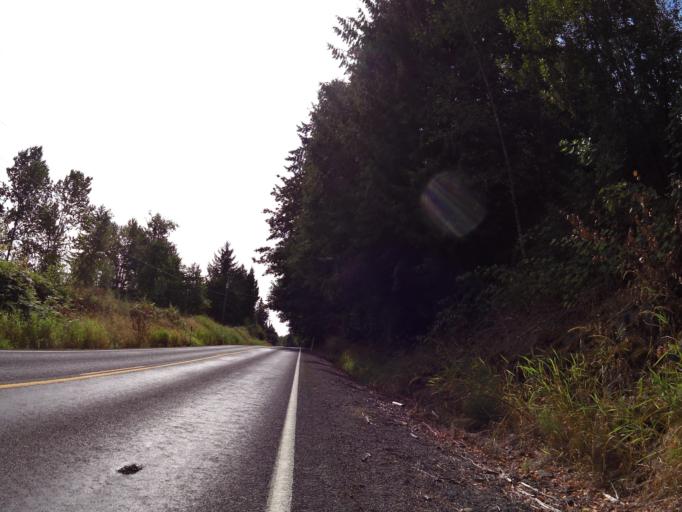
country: US
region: Washington
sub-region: Lewis County
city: Chehalis
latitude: 46.6334
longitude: -122.9704
